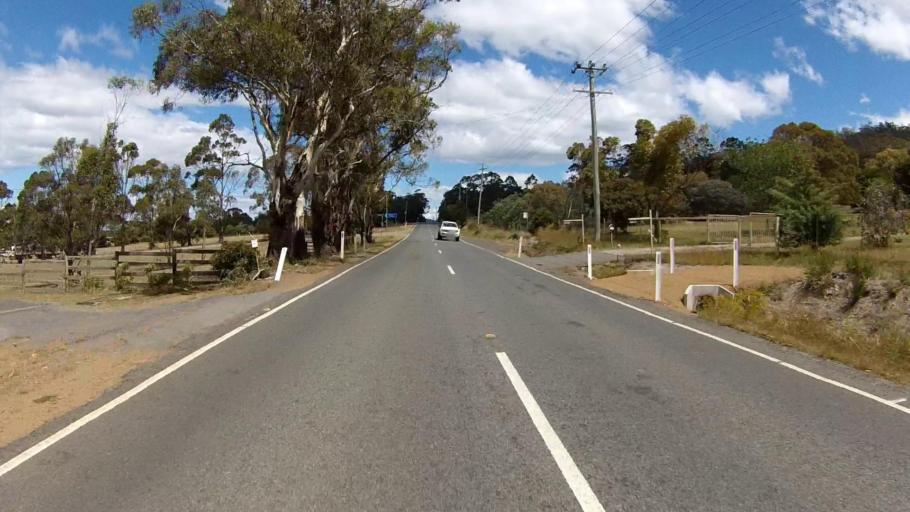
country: AU
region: Tasmania
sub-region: Clarence
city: Acton Park
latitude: -42.8949
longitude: 147.4814
